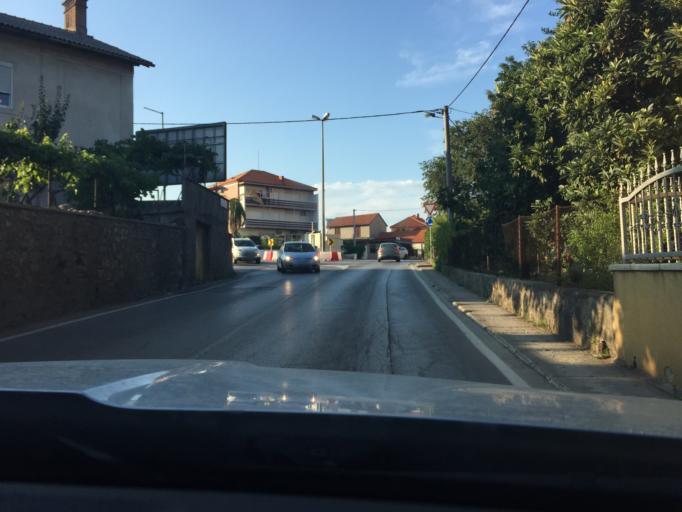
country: HR
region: Zadarska
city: Zadar
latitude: 44.1238
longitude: 15.2329
